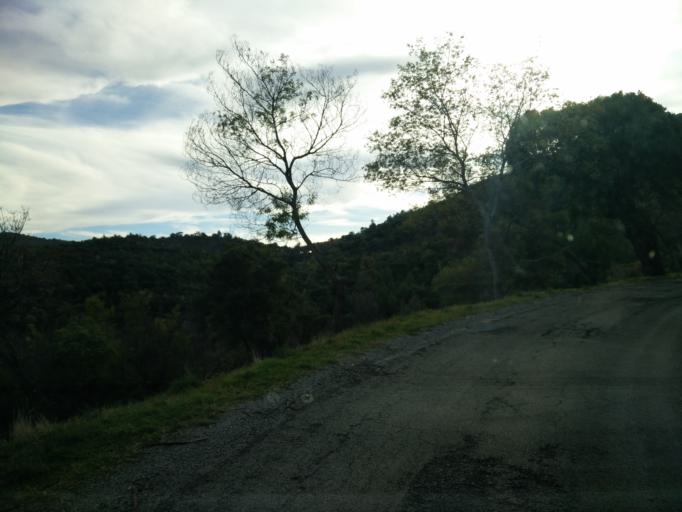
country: FR
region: Provence-Alpes-Cote d'Azur
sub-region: Departement du Var
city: Roquebrune-sur-Argens
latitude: 43.4236
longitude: 6.6387
